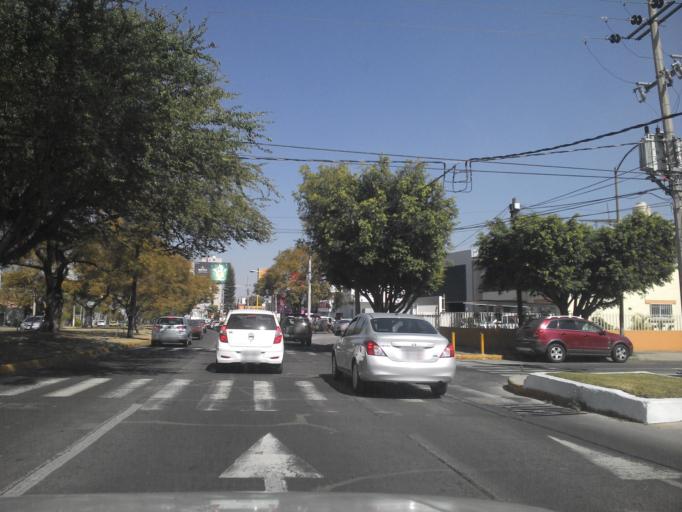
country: MX
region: Jalisco
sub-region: Zapopan
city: Zapopan
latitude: 20.7000
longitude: -103.3679
